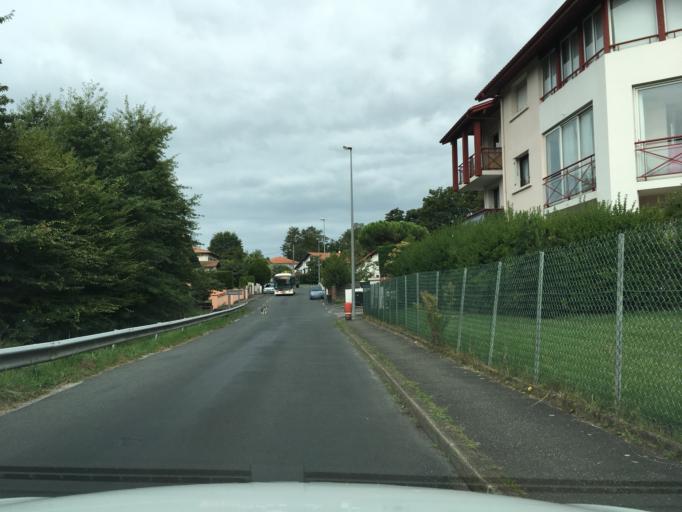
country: FR
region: Aquitaine
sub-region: Departement des Pyrenees-Atlantiques
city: Bayonne
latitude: 43.4958
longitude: -1.5002
